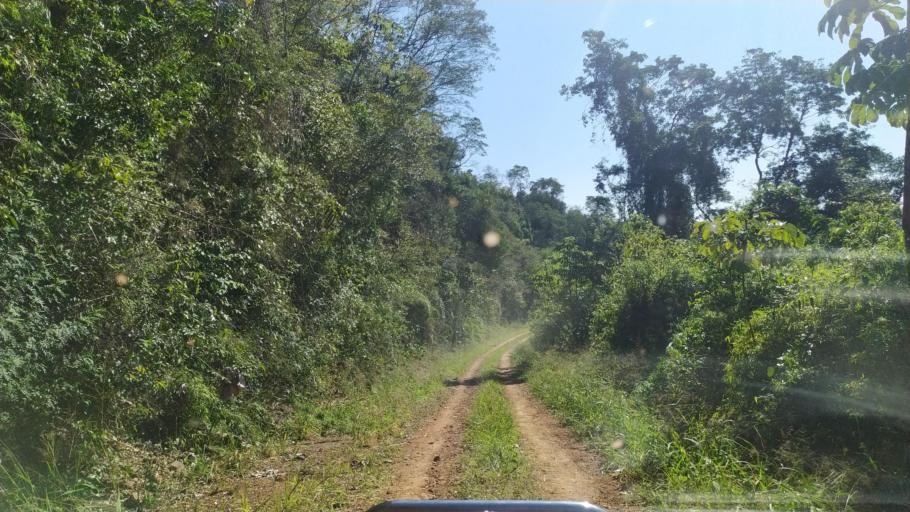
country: AR
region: Misiones
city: El Alcazar
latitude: -26.7640
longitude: -54.5771
